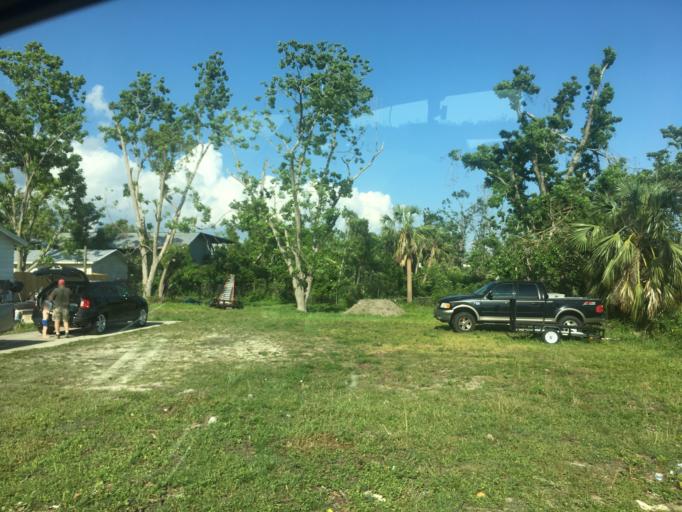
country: US
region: Florida
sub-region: Bay County
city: Cedar Grove
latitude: 30.1537
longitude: -85.6356
